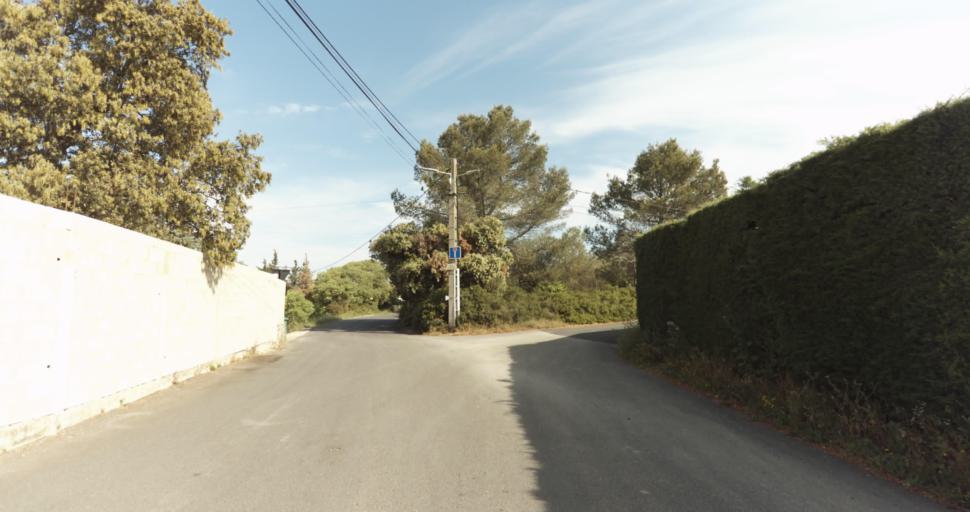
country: FR
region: Languedoc-Roussillon
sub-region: Departement du Gard
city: Poulx
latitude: 43.8715
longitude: 4.3937
